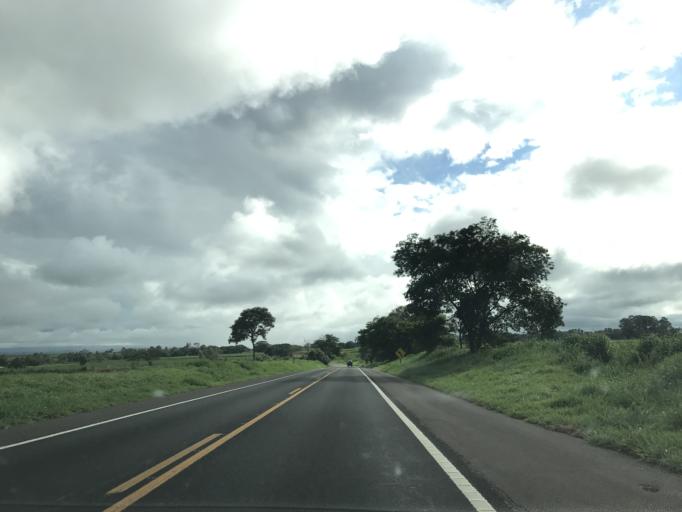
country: BR
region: Sao Paulo
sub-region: Penapolis
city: Penapolis
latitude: -21.4850
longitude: -50.2114
